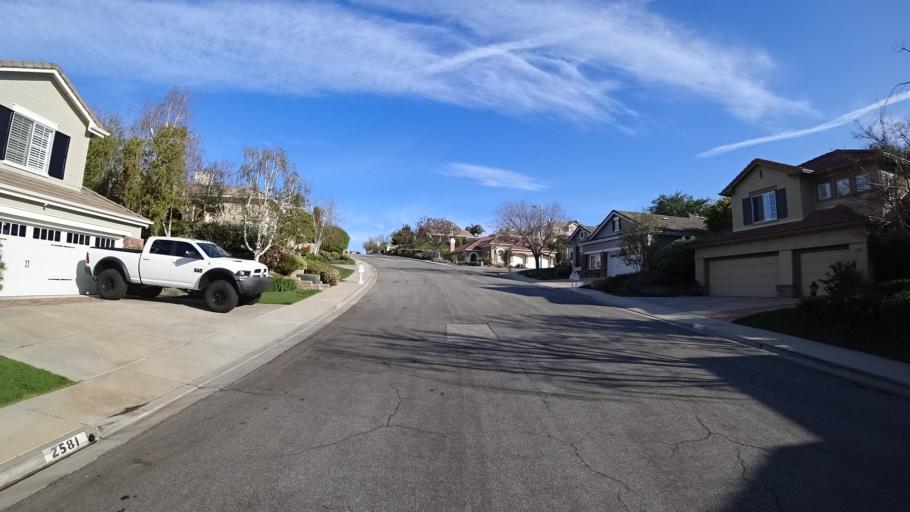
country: US
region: California
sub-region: Ventura County
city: Thousand Oaks
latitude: 34.2139
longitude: -118.8120
